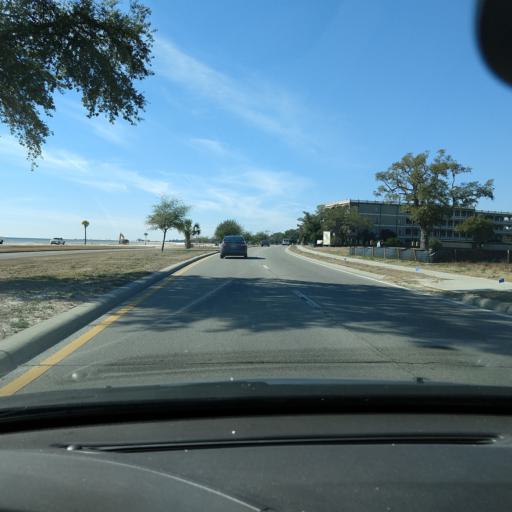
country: US
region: Mississippi
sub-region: Harrison County
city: Gulfport
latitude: 30.3572
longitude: -89.1153
